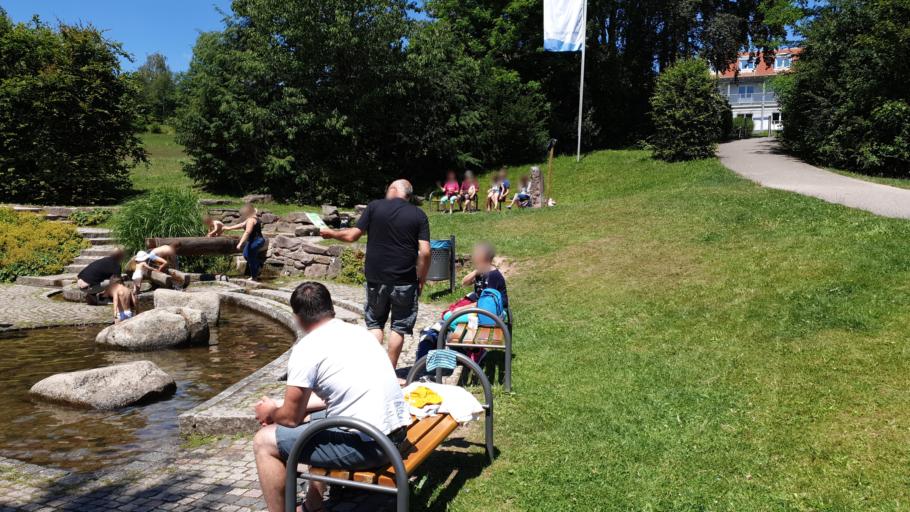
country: DE
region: Baden-Wuerttemberg
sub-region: Karlsruhe Region
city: Lossburg
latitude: 48.4115
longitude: 8.4452
